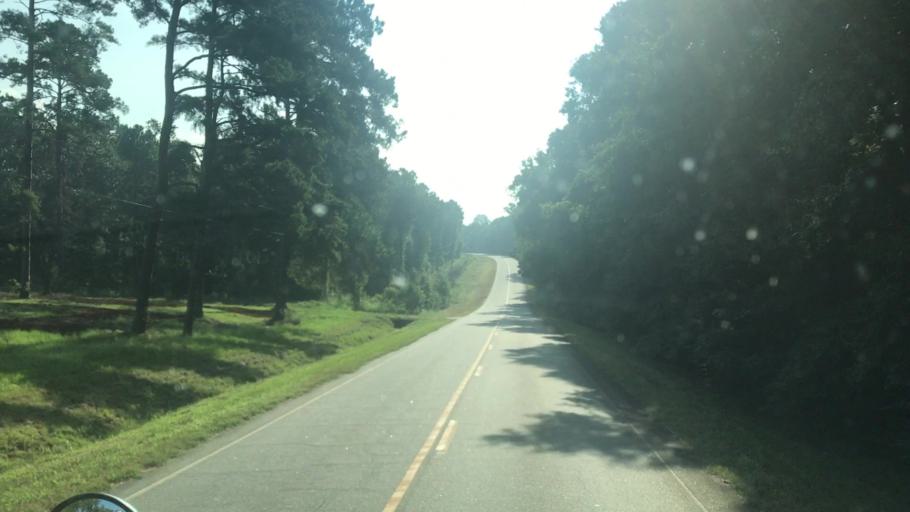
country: US
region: Florida
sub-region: Gadsden County
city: Quincy
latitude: 30.7001
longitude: -84.5248
